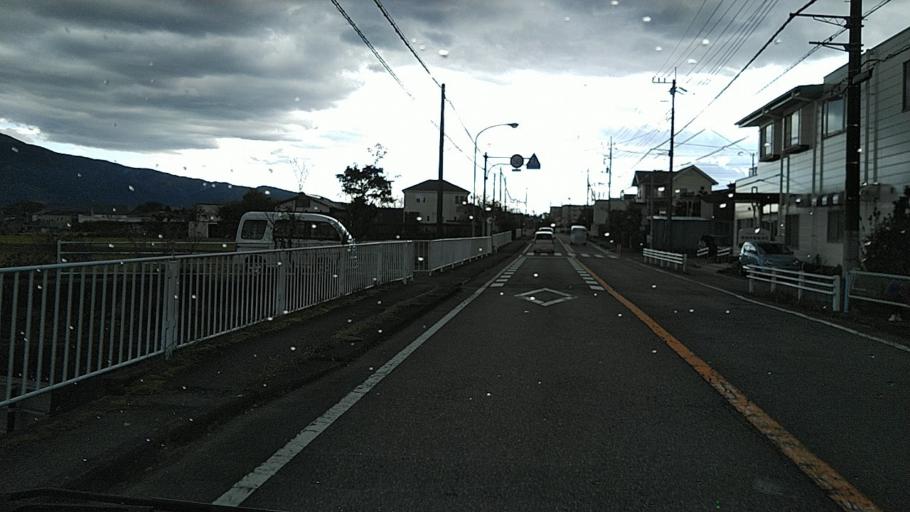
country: JP
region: Shizuoka
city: Gotemba
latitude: 35.3218
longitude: 138.9430
